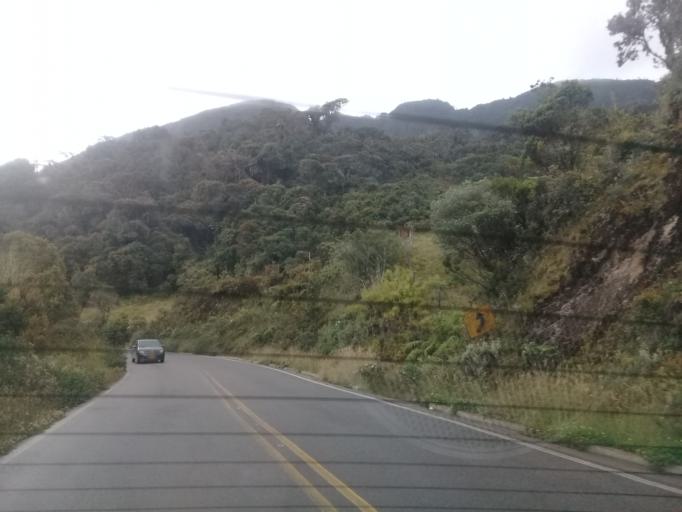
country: CO
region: Cundinamarca
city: Guatavita
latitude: 4.8586
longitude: -73.7545
